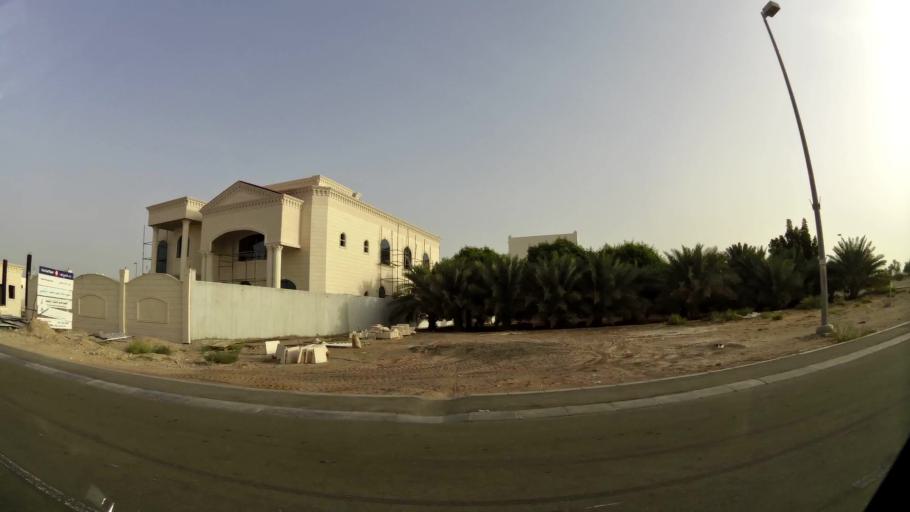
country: AE
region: Abu Dhabi
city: Al Ain
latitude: 24.1113
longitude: 55.7141
